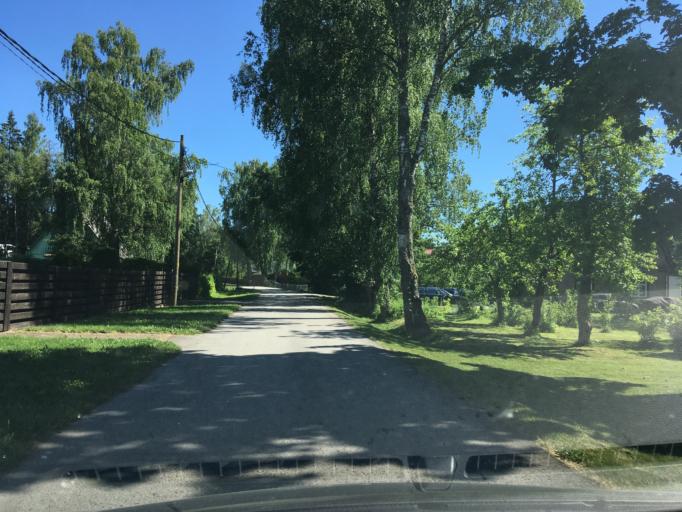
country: EE
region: Harju
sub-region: Raasiku vald
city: Raasiku
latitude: 59.1896
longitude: 25.1717
